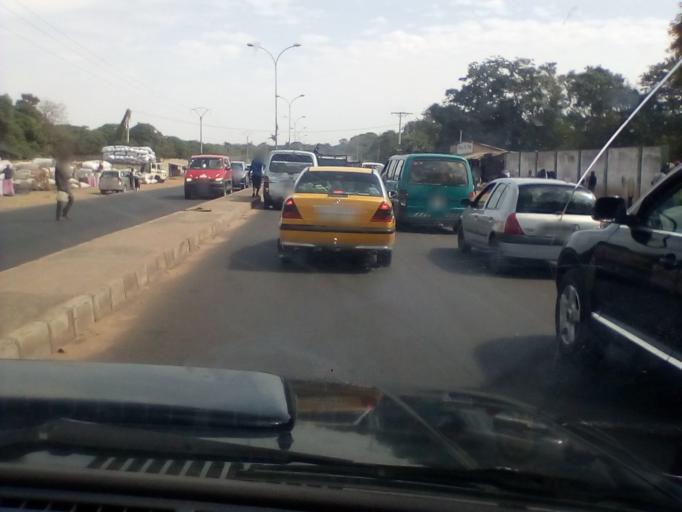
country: GM
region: Western
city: Abuko
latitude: 13.3996
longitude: -16.6506
